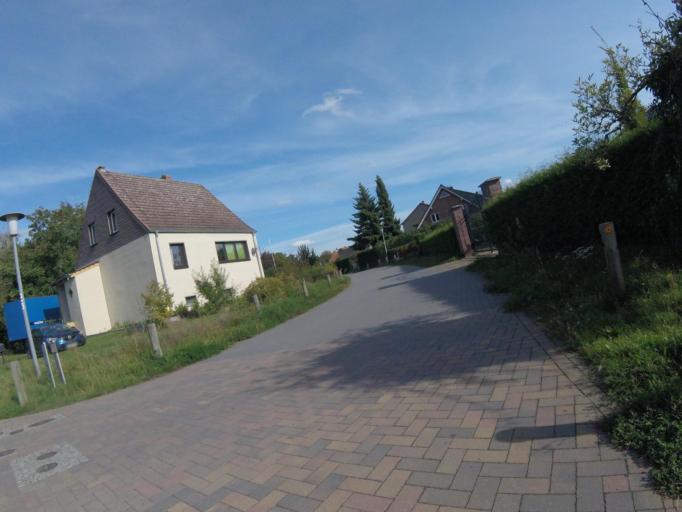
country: DE
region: Brandenburg
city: Bestensee
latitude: 52.2958
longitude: 13.7143
